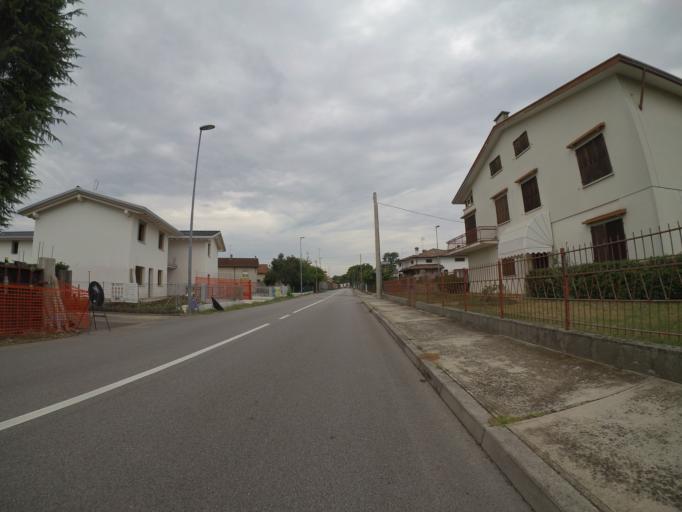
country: IT
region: Friuli Venezia Giulia
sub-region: Provincia di Udine
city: Codroipo
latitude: 45.9631
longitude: 12.9901
